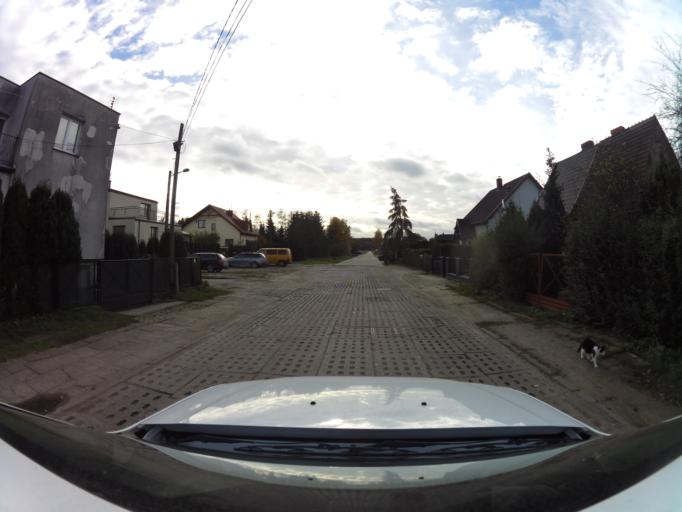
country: PL
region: West Pomeranian Voivodeship
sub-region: Powiat gryficki
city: Gryfice
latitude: 53.9170
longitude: 15.1800
